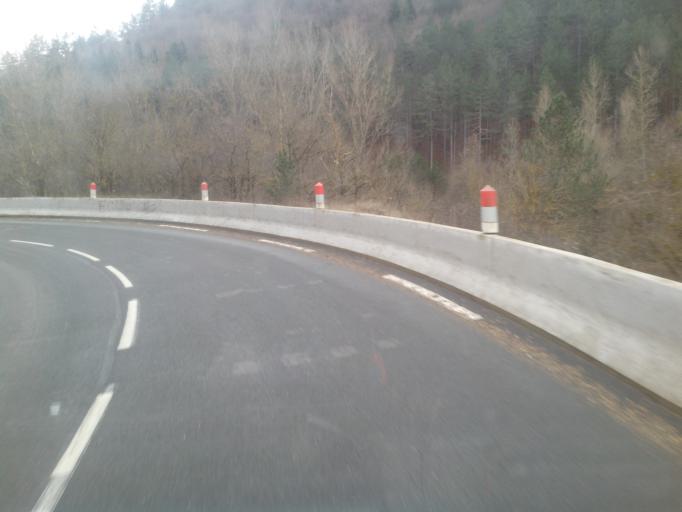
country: FR
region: Languedoc-Roussillon
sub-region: Departement de la Lozere
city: Mende
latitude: 44.4762
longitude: 3.4636
